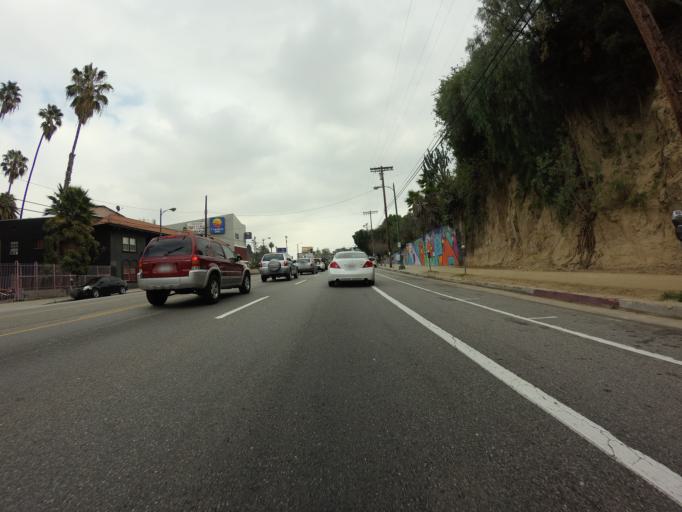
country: US
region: California
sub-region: Los Angeles County
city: Silver Lake
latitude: 34.0813
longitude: -118.2712
